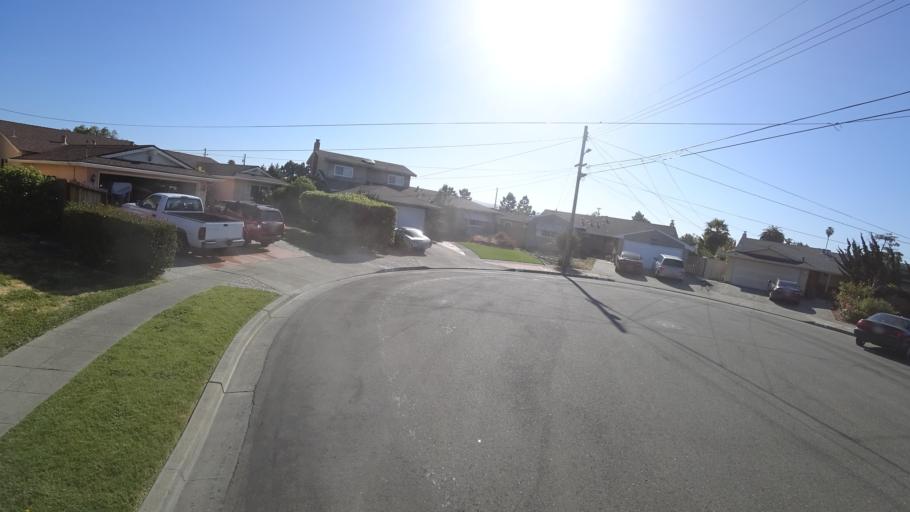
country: US
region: California
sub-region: Alameda County
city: Hayward
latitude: 37.6189
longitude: -122.0913
